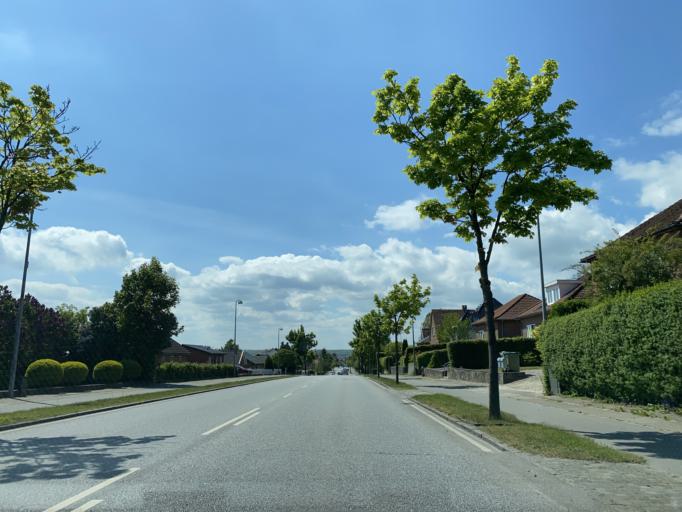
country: DK
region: South Denmark
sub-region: Aabenraa Kommune
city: Aabenraa
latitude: 55.0584
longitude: 9.4308
